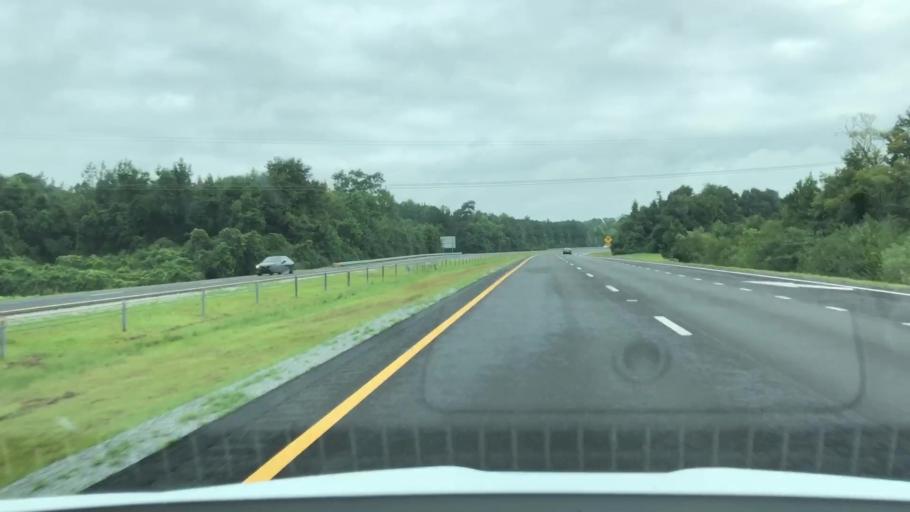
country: US
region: North Carolina
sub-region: Wayne County
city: Fremont
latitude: 35.5001
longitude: -77.9985
